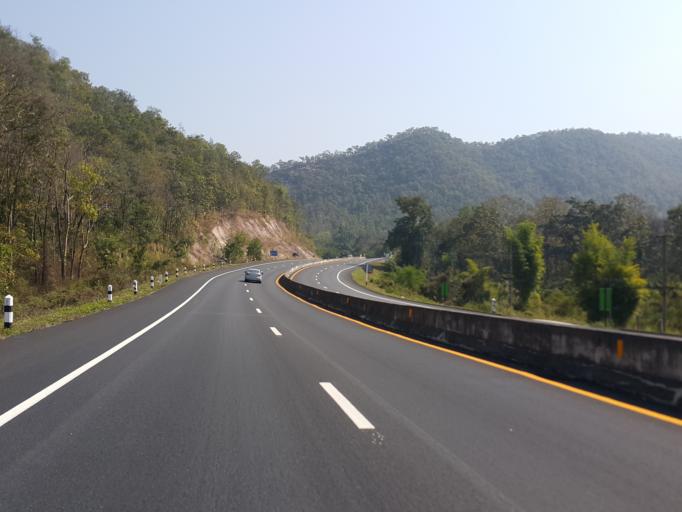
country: TH
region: Chiang Mai
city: San Sai
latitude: 18.8932
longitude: 99.1723
